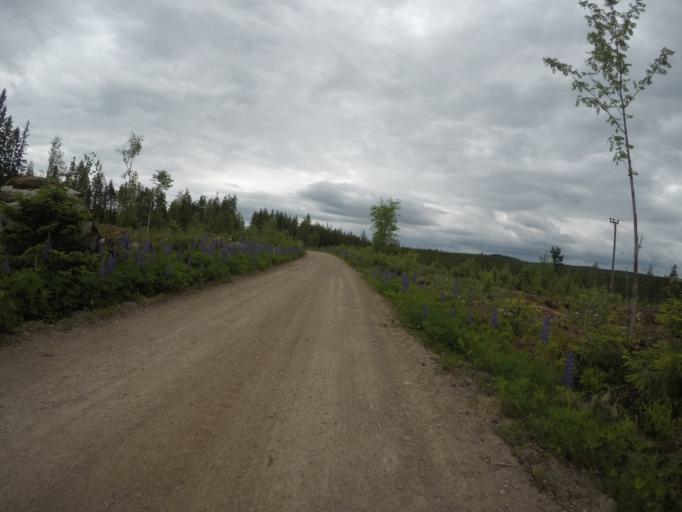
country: SE
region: Dalarna
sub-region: Ludvika Kommun
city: Abborrberget
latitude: 60.0887
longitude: 14.5495
